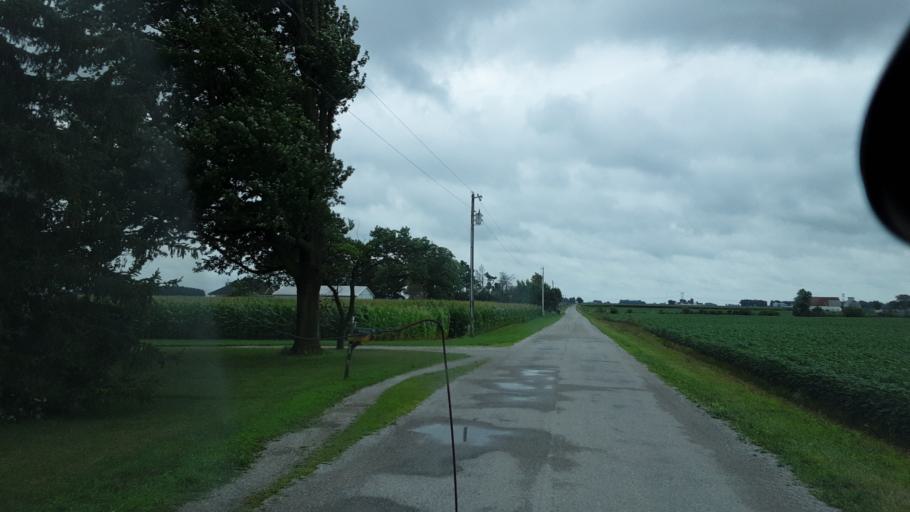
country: US
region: Indiana
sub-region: Wells County
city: Bluffton
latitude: 40.7770
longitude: -85.0714
